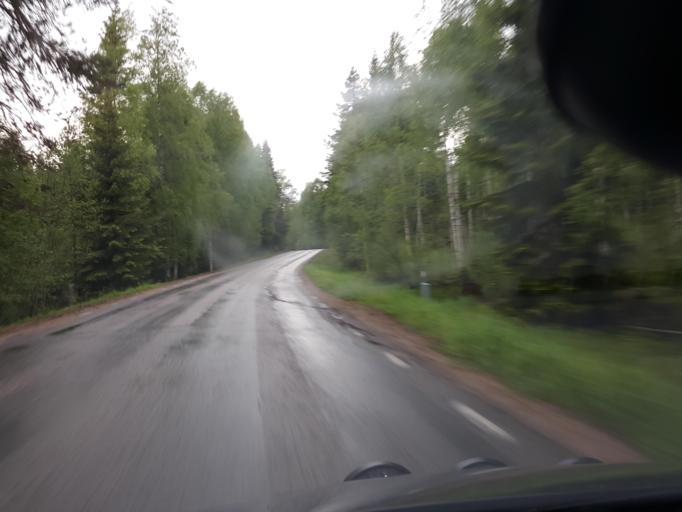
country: SE
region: Gaevleborg
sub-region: Ljusdals Kommun
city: Jaervsoe
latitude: 61.8007
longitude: 16.1751
